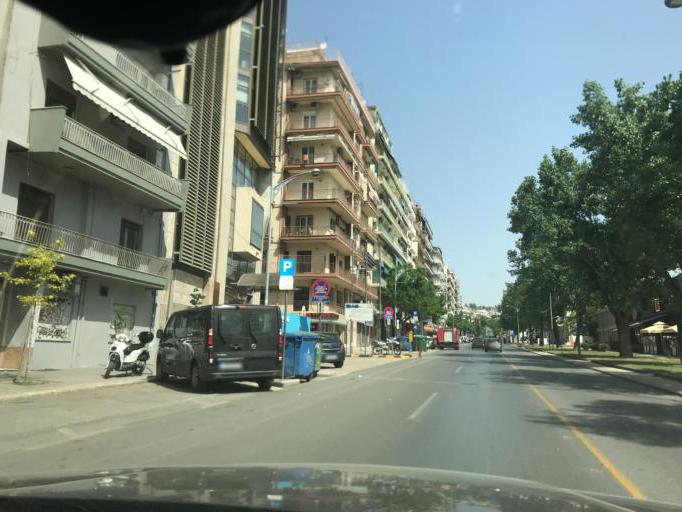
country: GR
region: Central Macedonia
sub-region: Nomos Thessalonikis
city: Agios Pavlos
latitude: 40.6282
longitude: 22.9532
